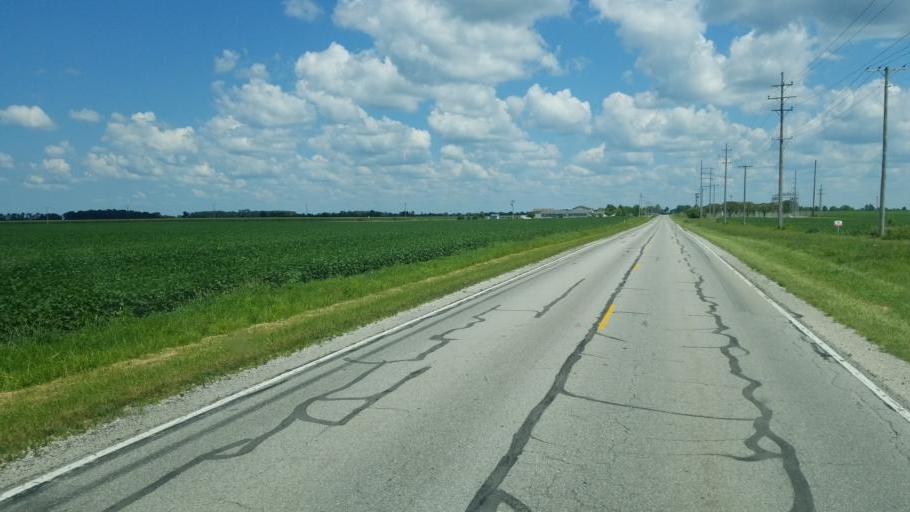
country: US
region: Ohio
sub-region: Marion County
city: Marion
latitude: 40.6303
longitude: -83.0554
